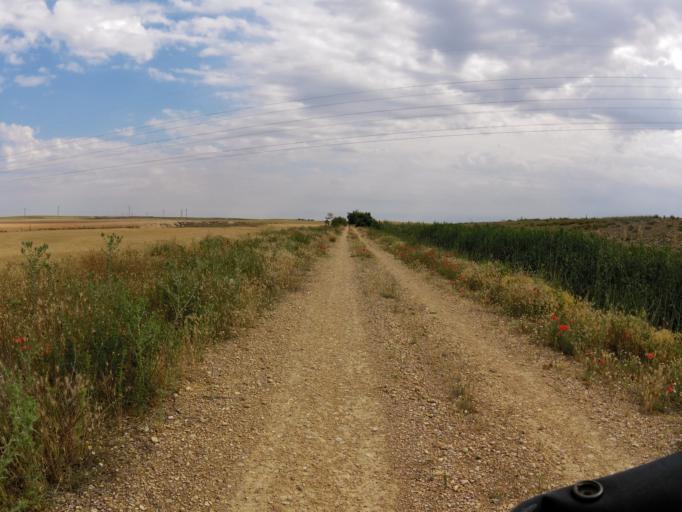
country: ES
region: Castille-La Mancha
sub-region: Provincia de Albacete
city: Albacete
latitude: 39.0355
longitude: -1.7889
